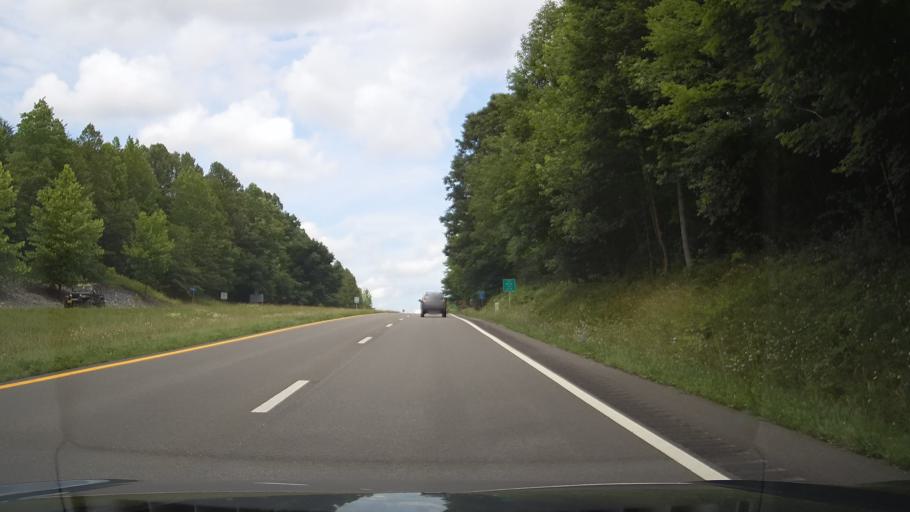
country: US
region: Virginia
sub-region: Wise County
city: Big Stone Gap
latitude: 36.8115
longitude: -82.7876
